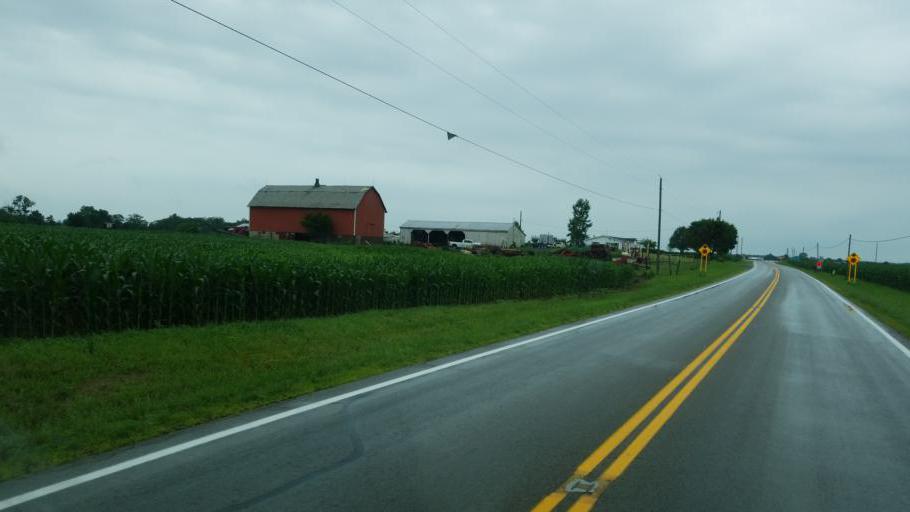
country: US
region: Ohio
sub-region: Hardin County
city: Kenton
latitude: 40.5287
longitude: -83.5713
